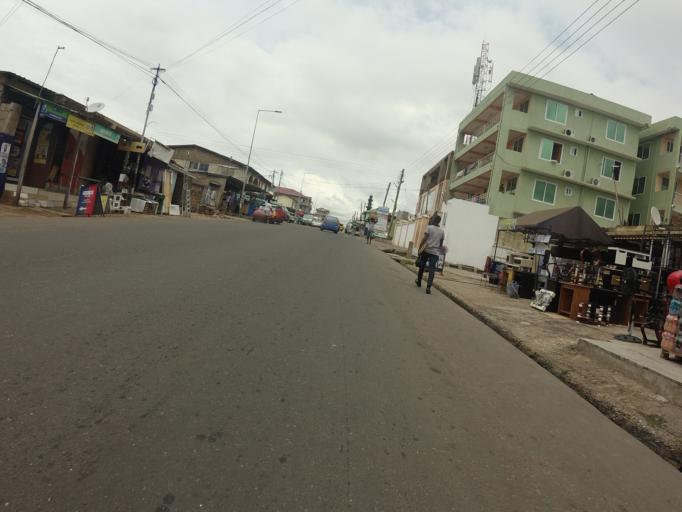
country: GH
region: Greater Accra
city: Accra
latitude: 5.5804
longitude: -0.2055
